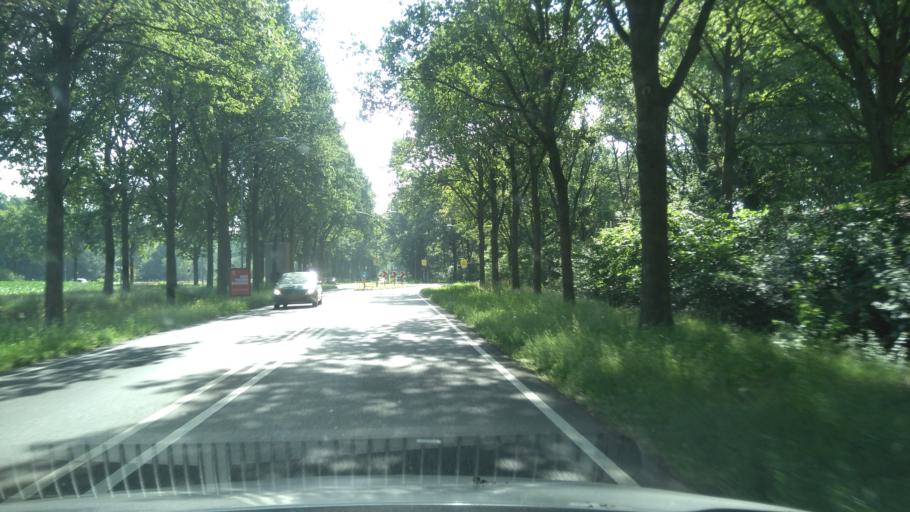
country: NL
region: North Brabant
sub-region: Gemeente Goirle
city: Goirle
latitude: 51.5292
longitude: 5.0574
